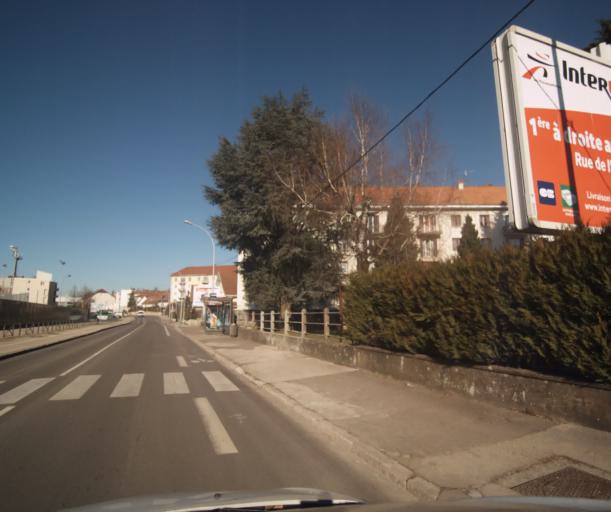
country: FR
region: Franche-Comte
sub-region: Departement du Doubs
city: Besancon
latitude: 47.2444
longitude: 6.0043
